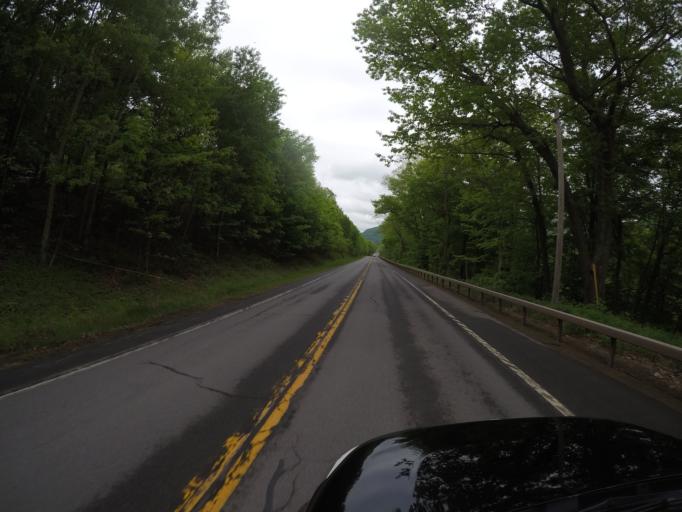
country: US
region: New York
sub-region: Delaware County
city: Delhi
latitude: 42.2557
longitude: -74.9198
